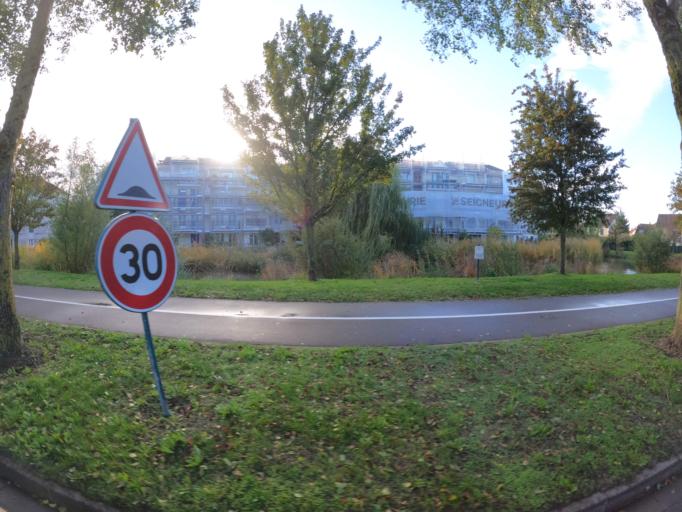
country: FR
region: Ile-de-France
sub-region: Departement de Seine-et-Marne
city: Bailly-Romainvilliers
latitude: 48.8500
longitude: 2.8155
